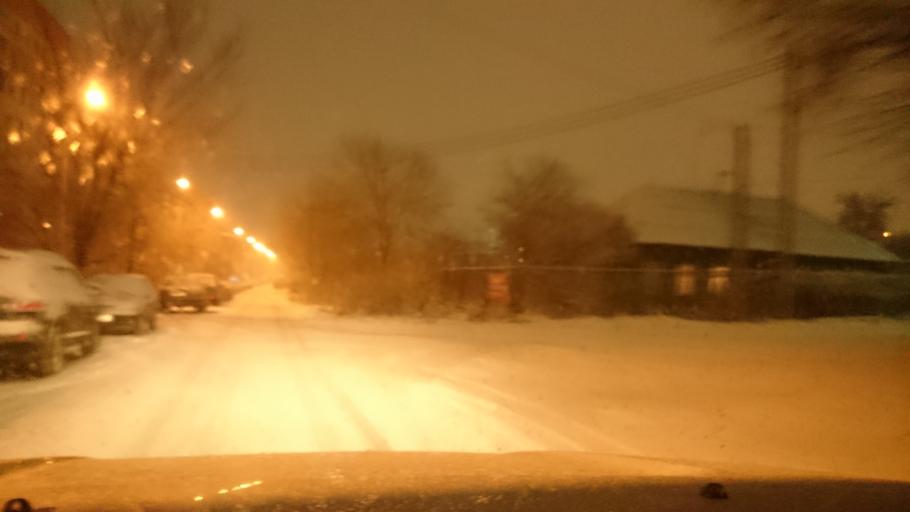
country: RU
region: Tula
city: Mendeleyevskiy
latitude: 54.1826
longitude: 37.5688
